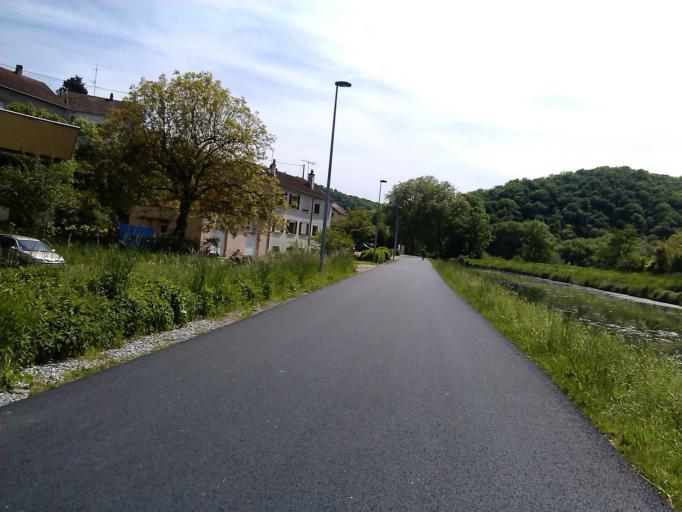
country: FR
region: Franche-Comte
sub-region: Departement du Doubs
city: Avanne-Aveney
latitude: 47.1963
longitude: 5.9593
